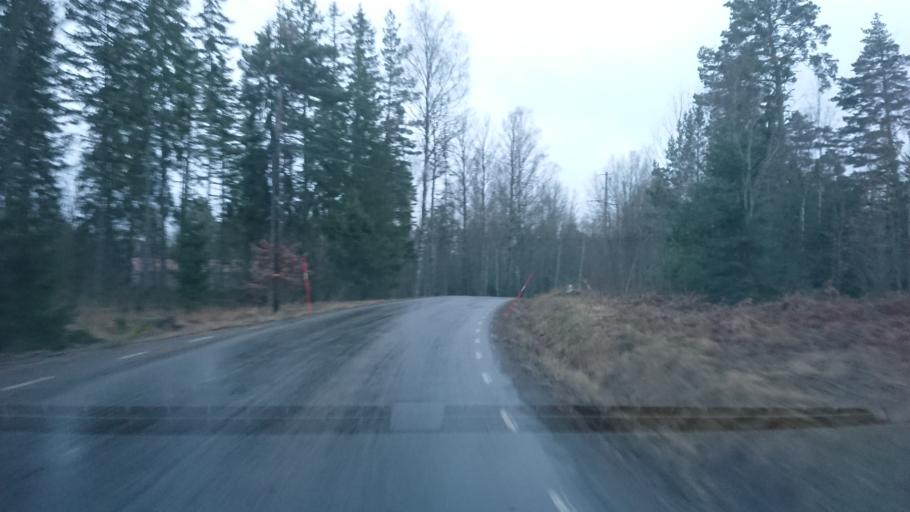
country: SE
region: Uppsala
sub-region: Osthammars Kommun
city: Bjorklinge
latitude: 59.9980
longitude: 17.5959
